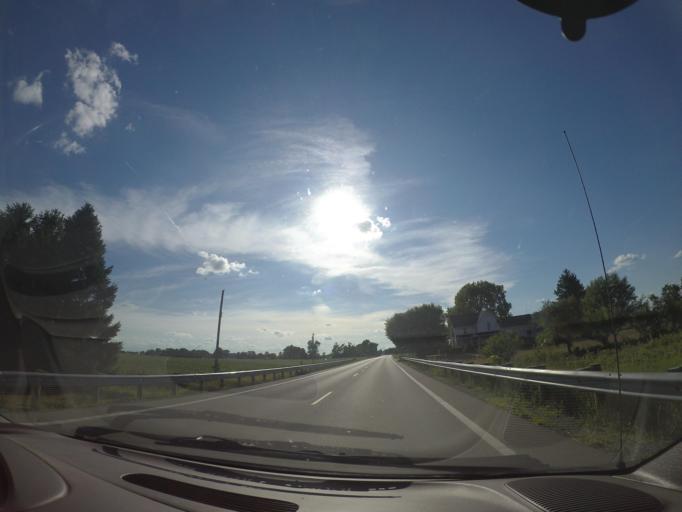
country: US
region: Ohio
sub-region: Fulton County
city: Archbold
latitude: 41.4350
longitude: -84.2394
